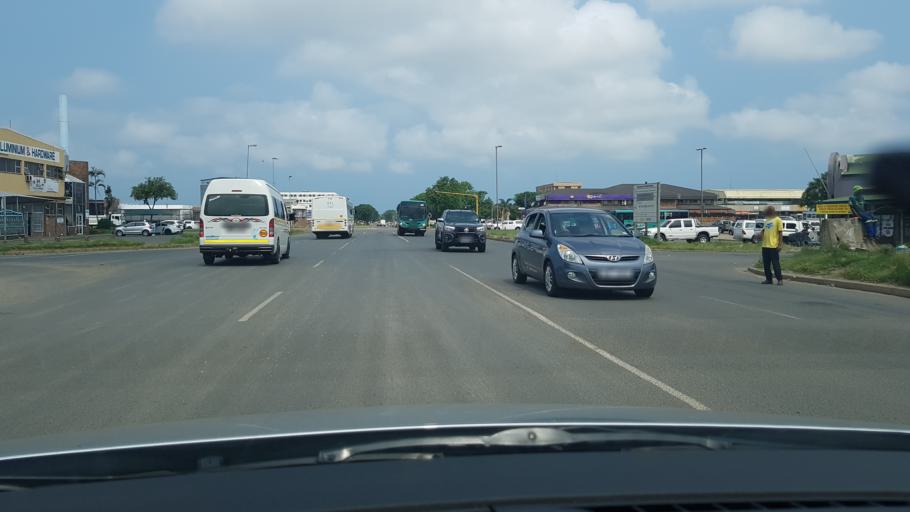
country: ZA
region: KwaZulu-Natal
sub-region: uThungulu District Municipality
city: Richards Bay
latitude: -28.7486
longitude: 32.0477
